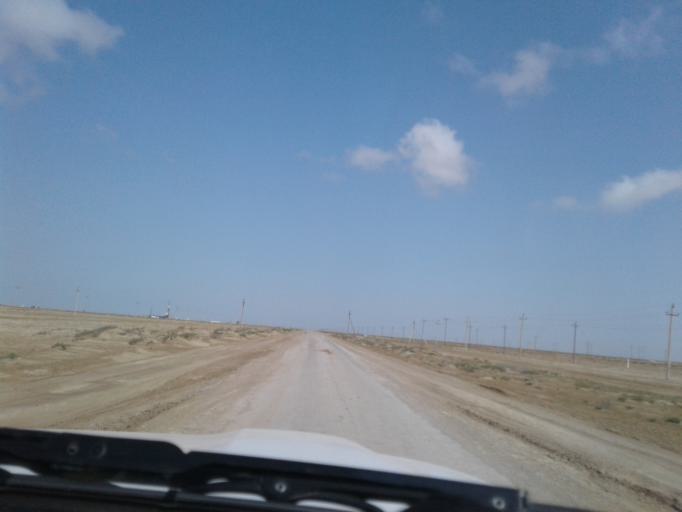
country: IR
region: Golestan
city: Gomishan
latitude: 37.7348
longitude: 53.9356
